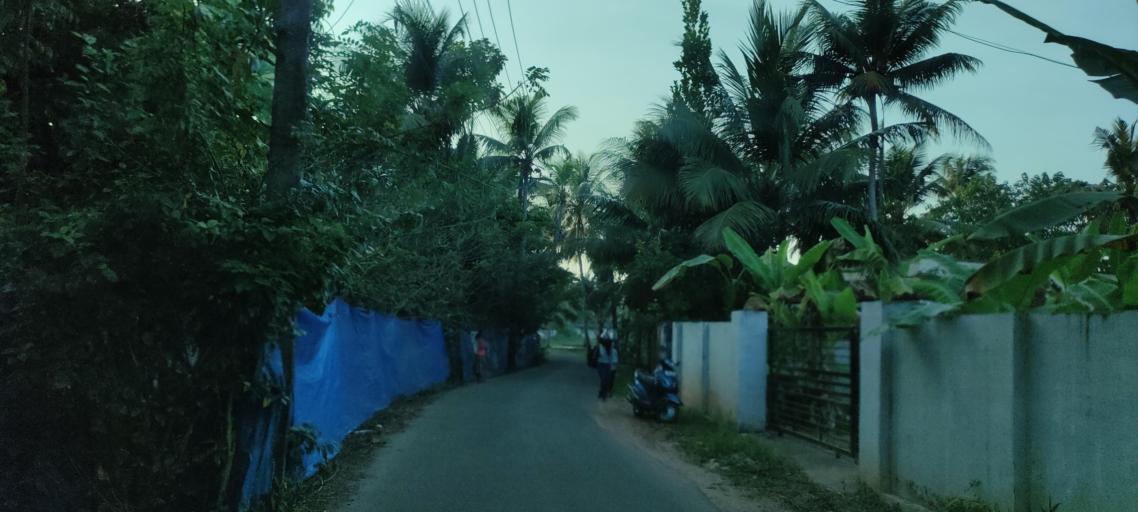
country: IN
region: Kerala
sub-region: Alappuzha
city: Kutiatodu
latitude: 9.7872
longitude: 76.3234
